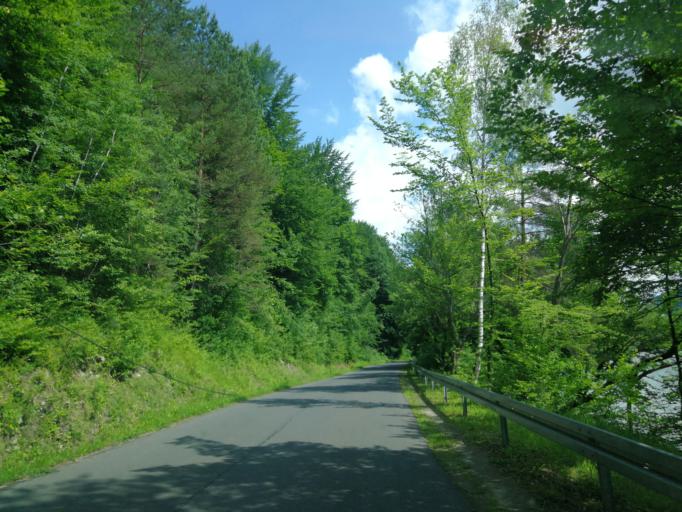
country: PL
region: Subcarpathian Voivodeship
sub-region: Powiat leski
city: Uherce Mineralne
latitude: 49.4274
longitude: 22.4194
